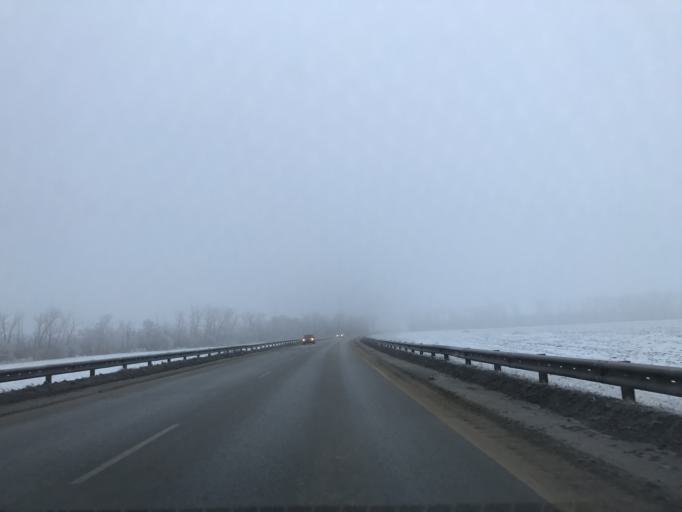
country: RU
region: Rostov
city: Temernik
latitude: 47.3744
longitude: 39.7967
